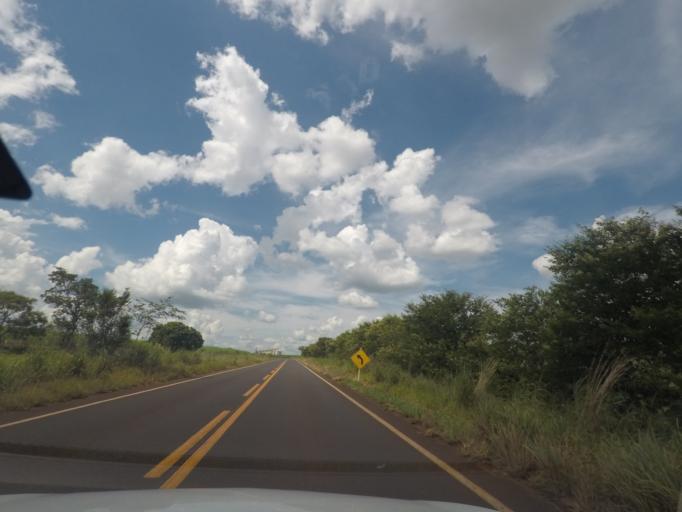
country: BR
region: Minas Gerais
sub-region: Conceicao Das Alagoas
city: Conceicao das Alagoas
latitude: -19.8136
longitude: -48.5858
